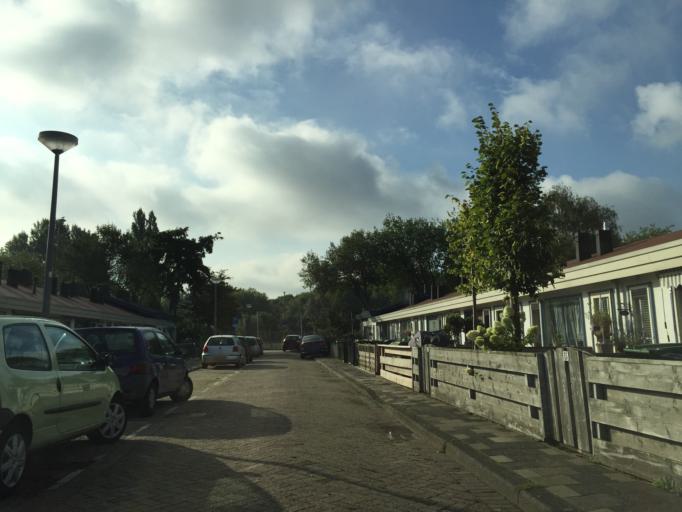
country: NL
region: South Holland
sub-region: Gemeente Rotterdam
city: Delfshaven
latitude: 51.9452
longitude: 4.4300
